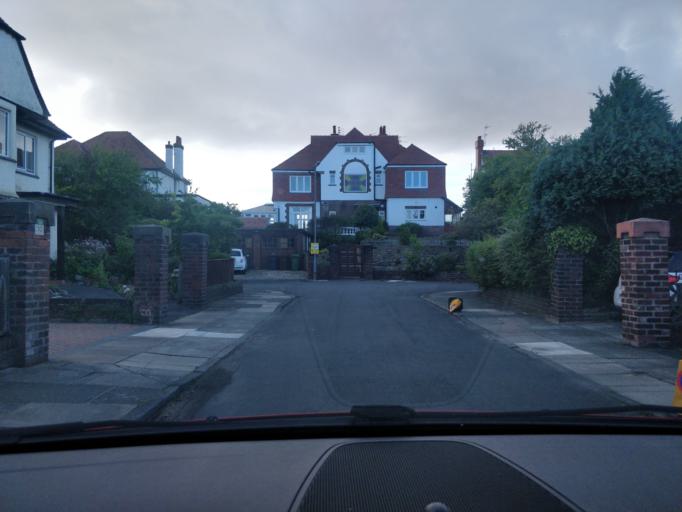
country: GB
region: England
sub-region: Sefton
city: Southport
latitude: 53.6442
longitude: -3.0152
